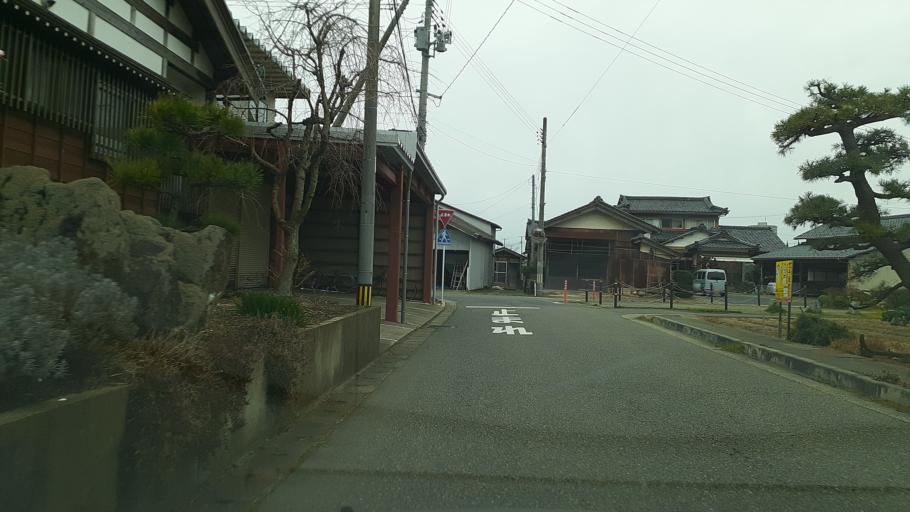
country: JP
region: Niigata
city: Niigata-shi
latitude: 37.8605
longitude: 139.0363
